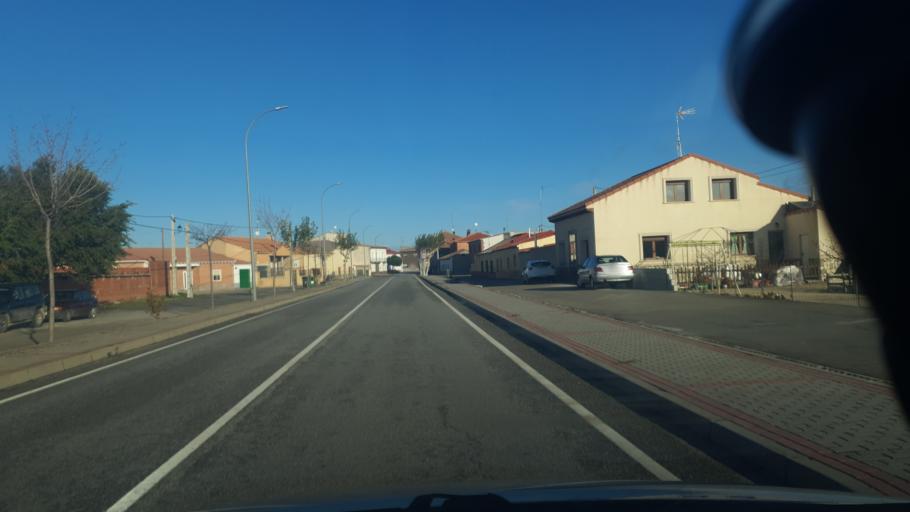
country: ES
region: Castille and Leon
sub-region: Provincia de Avila
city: Tinosillos
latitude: 40.9318
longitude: -4.7280
